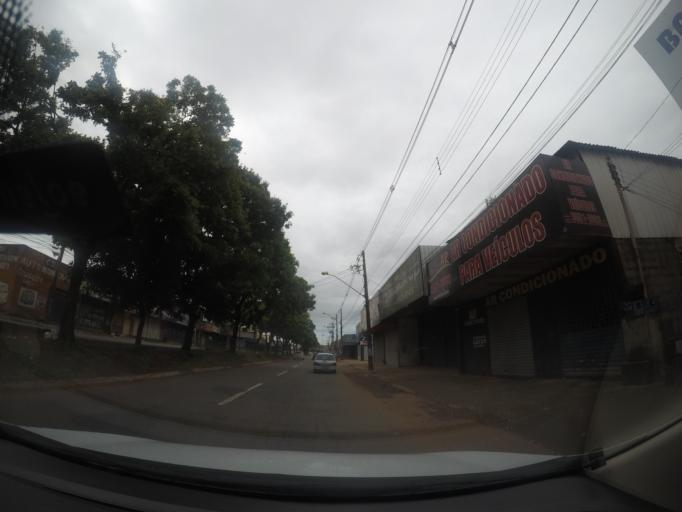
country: BR
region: Goias
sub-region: Goiania
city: Goiania
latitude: -16.6904
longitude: -49.3200
